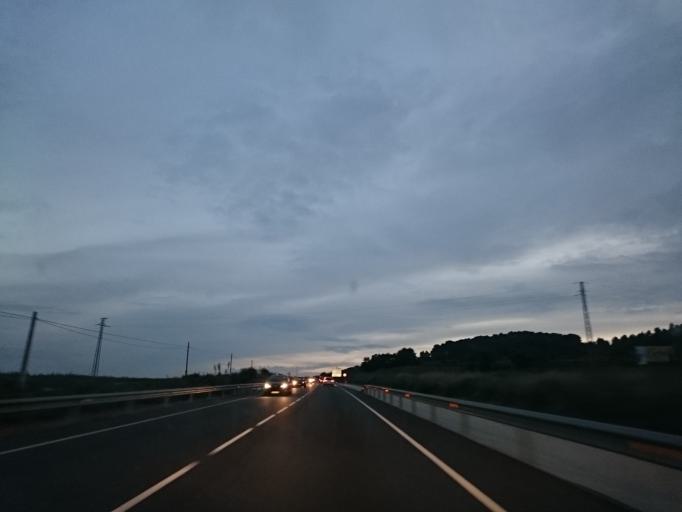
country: ES
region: Catalonia
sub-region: Provincia de Barcelona
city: La Granada
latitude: 41.3922
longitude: 1.7091
